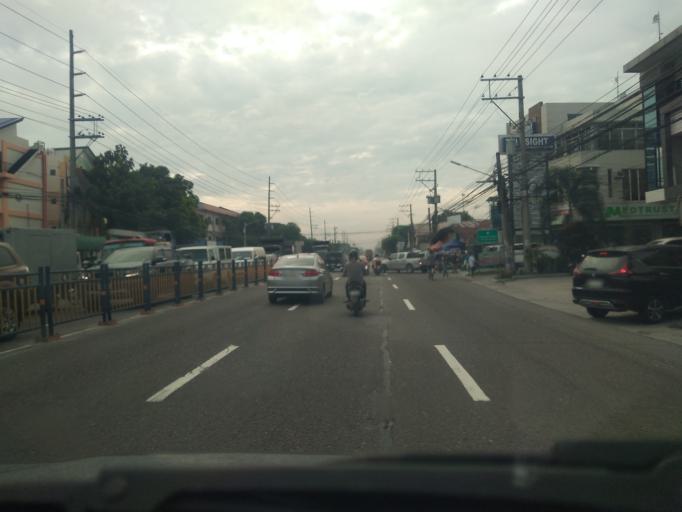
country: PH
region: Central Luzon
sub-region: Province of Pampanga
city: Bulaon
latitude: 15.0769
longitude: 120.6414
